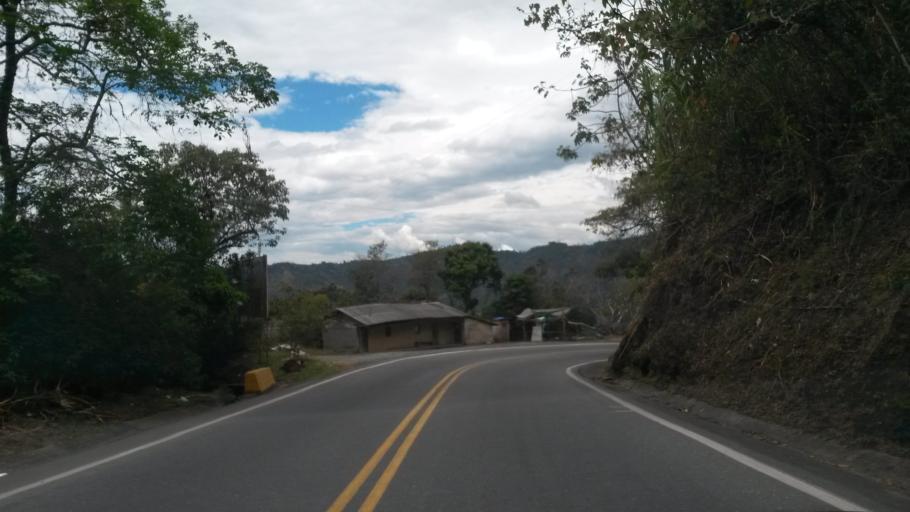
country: CO
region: Cauca
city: Rosas
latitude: 2.2726
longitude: -76.7262
